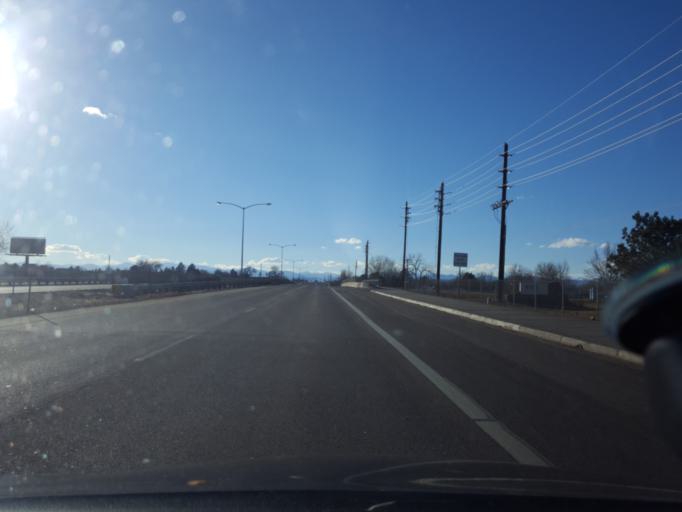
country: US
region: Colorado
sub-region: Adams County
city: Aurora
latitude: 39.7403
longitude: -104.7788
